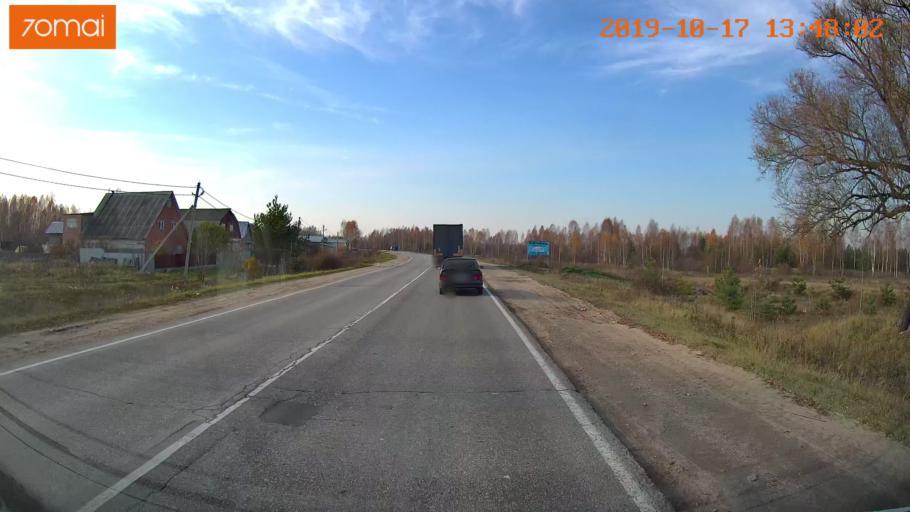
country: RU
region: Rjazan
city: Tuma
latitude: 55.1464
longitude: 40.4627
